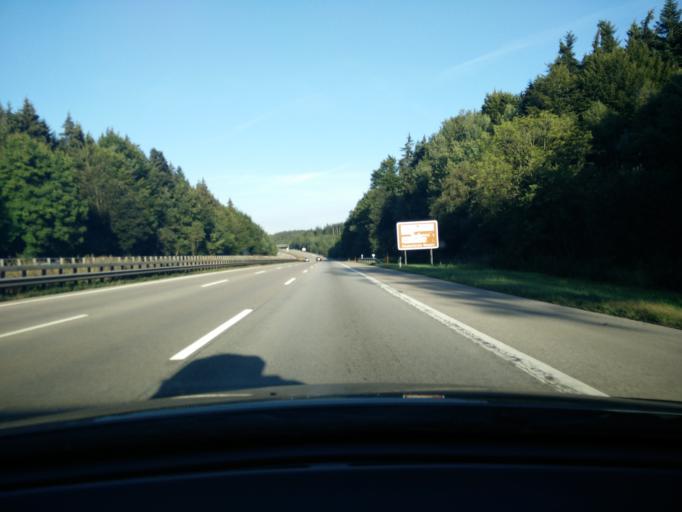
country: DE
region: Bavaria
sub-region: Upper Bavaria
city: Weyarn
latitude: 47.8630
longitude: 11.8362
